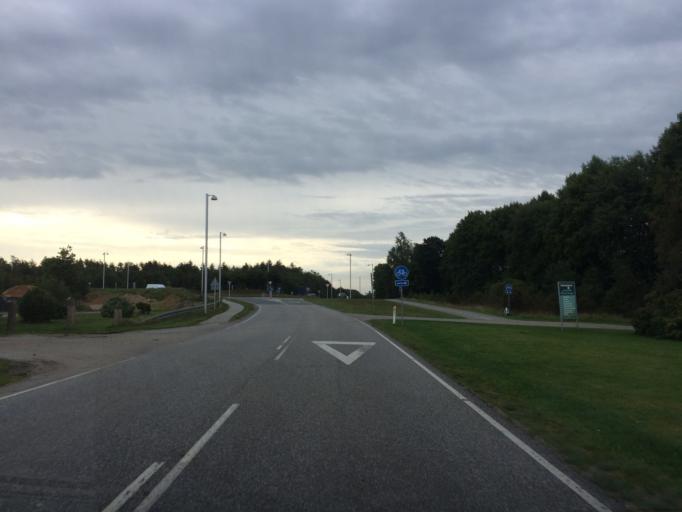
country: DK
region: Central Jutland
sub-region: Ikast-Brande Kommune
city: Brande
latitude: 55.9661
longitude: 9.0940
